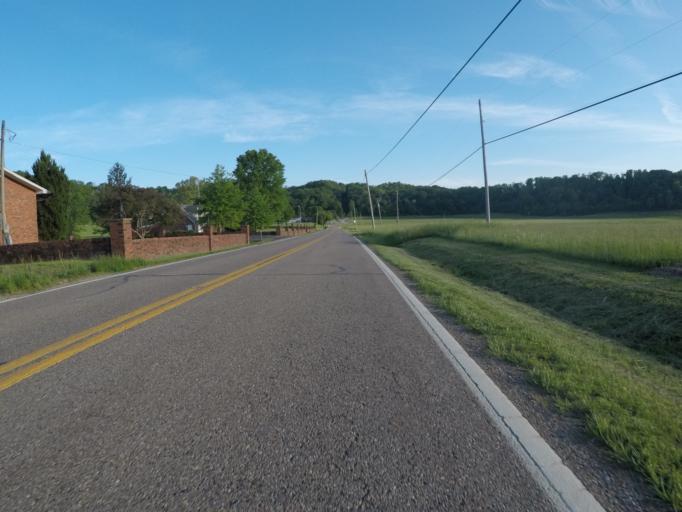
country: US
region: West Virginia
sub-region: Cabell County
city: Huntington
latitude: 38.5268
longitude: -82.4596
